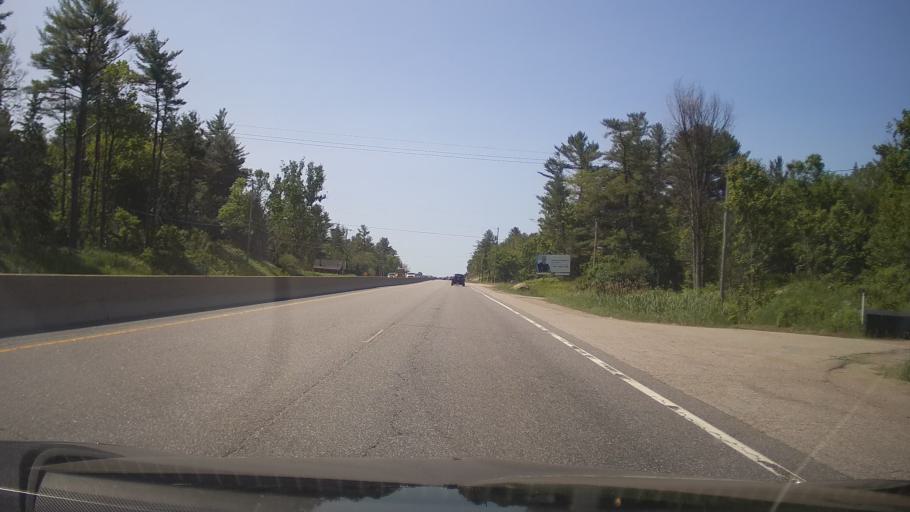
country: CA
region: Ontario
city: Gravenhurst
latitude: 44.8292
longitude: -79.3215
